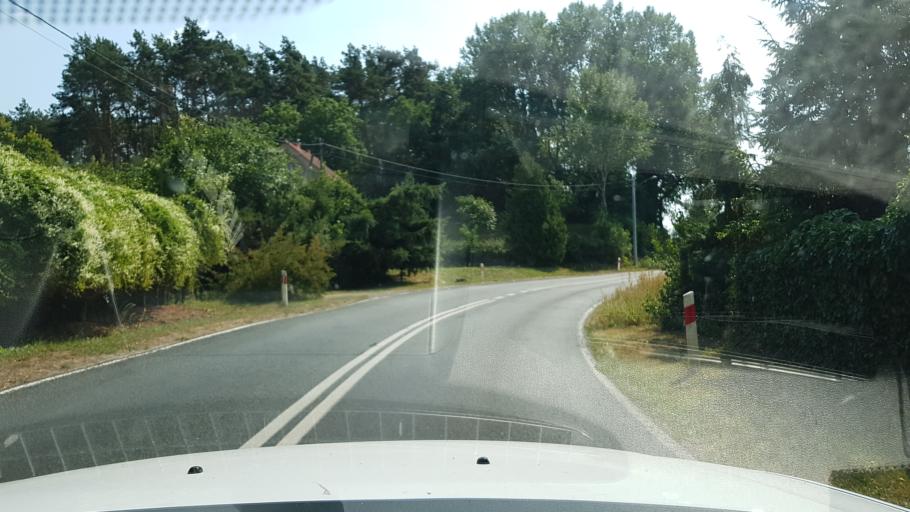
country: PL
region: West Pomeranian Voivodeship
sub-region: Powiat gryfinski
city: Cedynia
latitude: 52.8172
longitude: 14.2378
